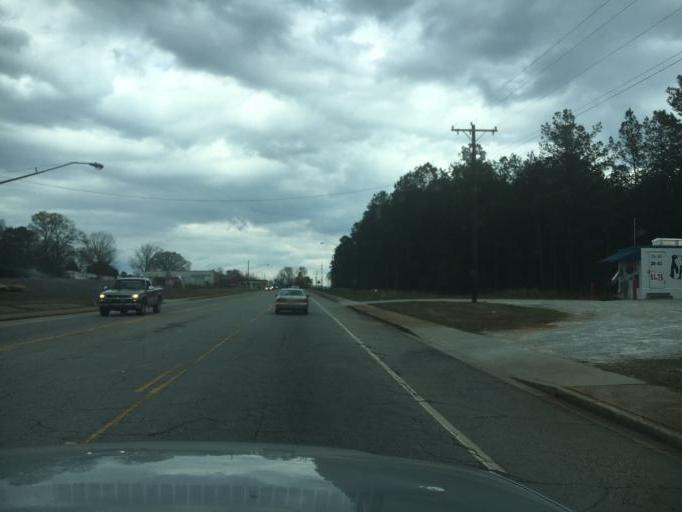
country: US
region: South Carolina
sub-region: Oconee County
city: Walhalla
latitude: 34.7571
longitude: -83.0455
